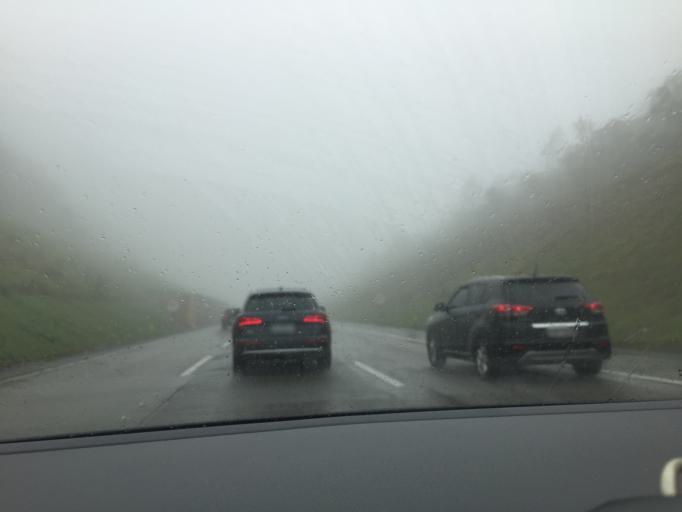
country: BR
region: Sao Paulo
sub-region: Cubatao
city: Cubatao
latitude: -23.9274
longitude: -46.5448
